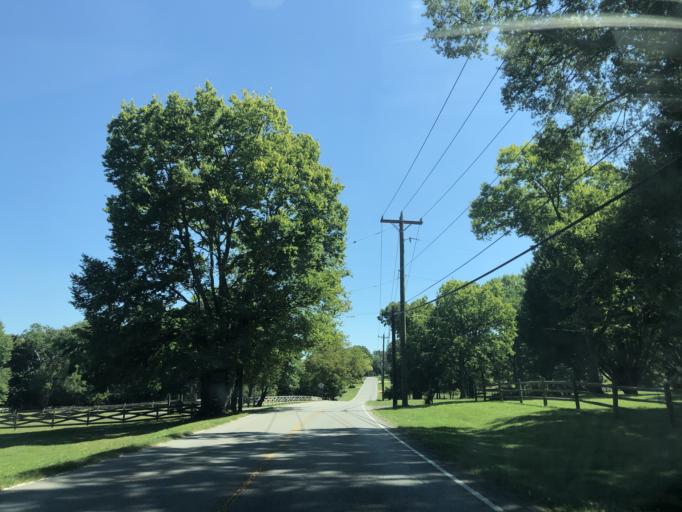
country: US
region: Tennessee
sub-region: Davidson County
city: Oak Hill
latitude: 36.0798
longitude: -86.7909
